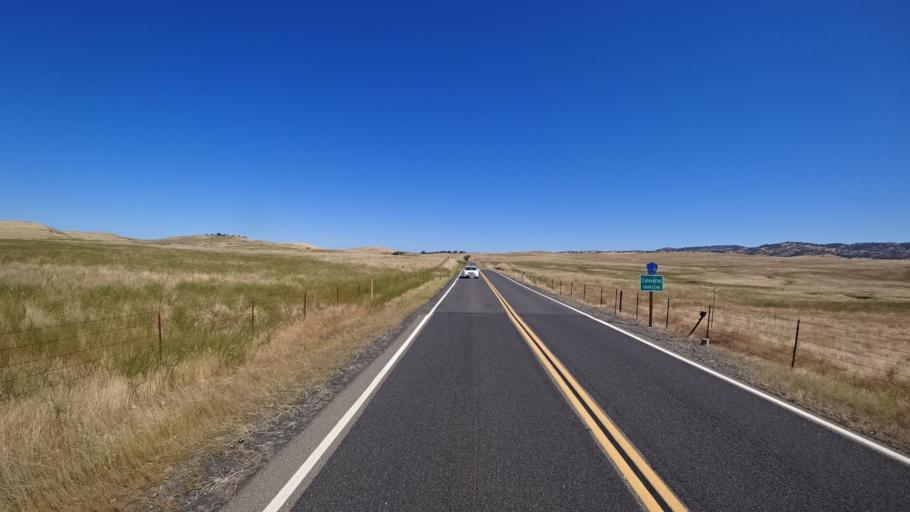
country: US
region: California
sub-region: Calaveras County
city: Rancho Calaveras
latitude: 38.0119
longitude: -120.8527
